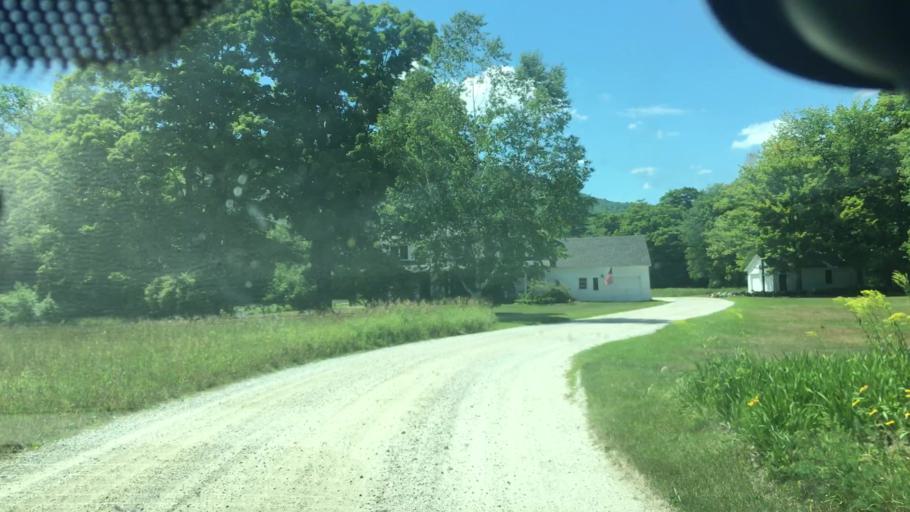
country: US
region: Vermont
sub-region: Windsor County
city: Chester
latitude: 43.4310
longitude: -72.7092
